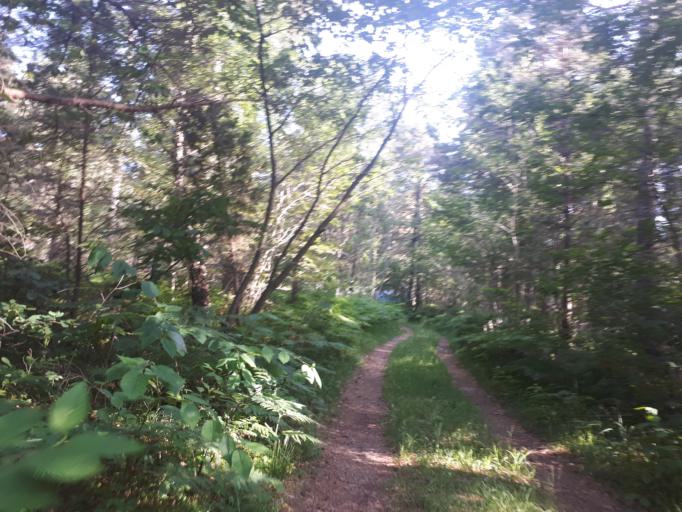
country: SE
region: Gotland
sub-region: Gotland
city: Visby
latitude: 57.6091
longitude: 18.2888
